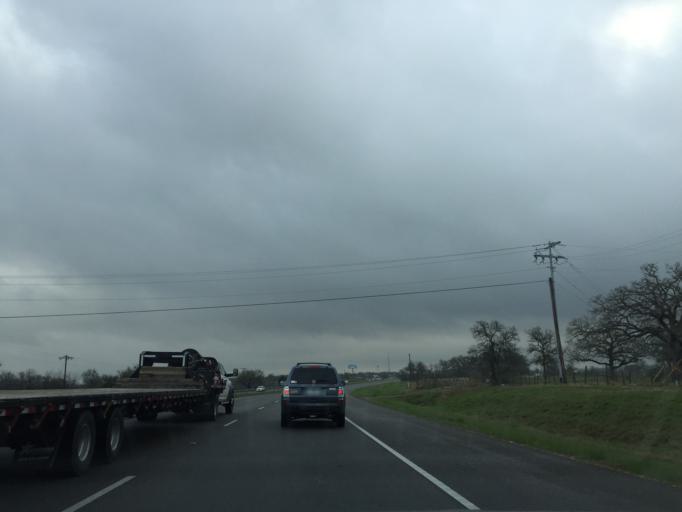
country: US
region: Texas
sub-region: Travis County
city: Garfield
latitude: 30.1896
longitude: -97.5771
